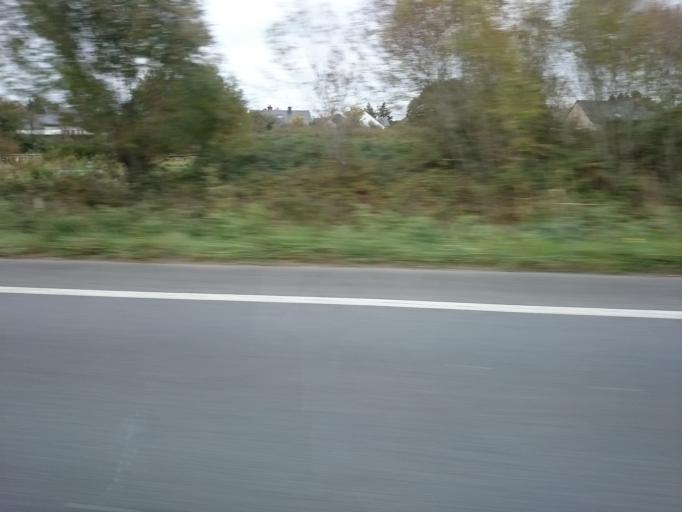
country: FR
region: Brittany
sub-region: Departement du Morbihan
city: Muzillac
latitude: 47.5639
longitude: -2.5084
